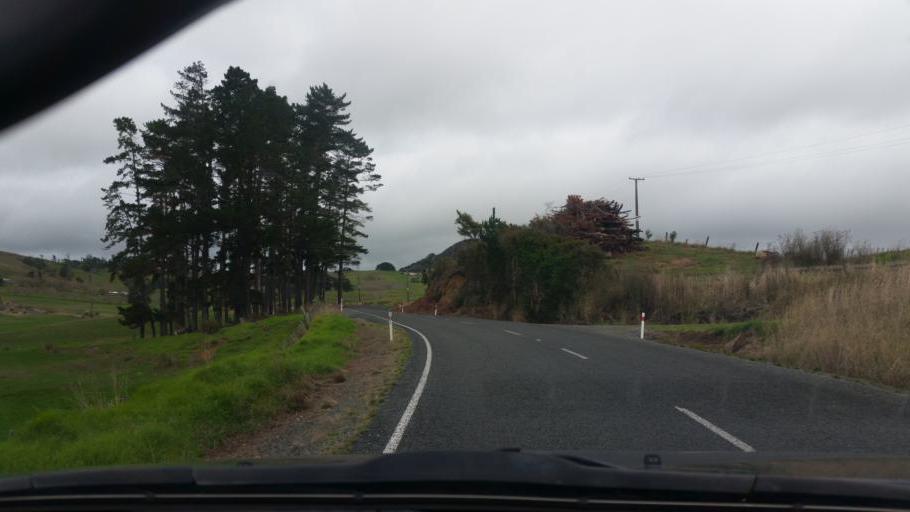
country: NZ
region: Northland
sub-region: Kaipara District
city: Dargaville
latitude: -36.0058
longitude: 173.9668
